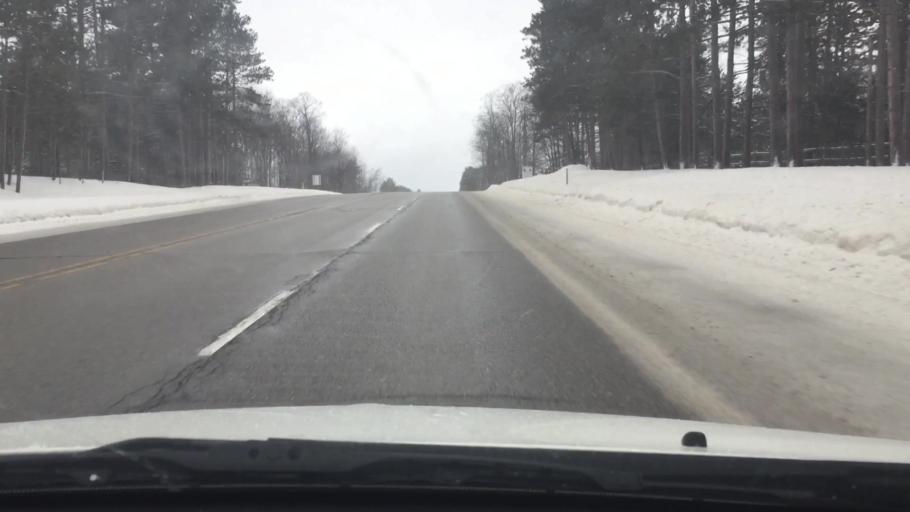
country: US
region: Michigan
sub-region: Otsego County
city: Gaylord
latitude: 45.0621
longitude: -84.8250
